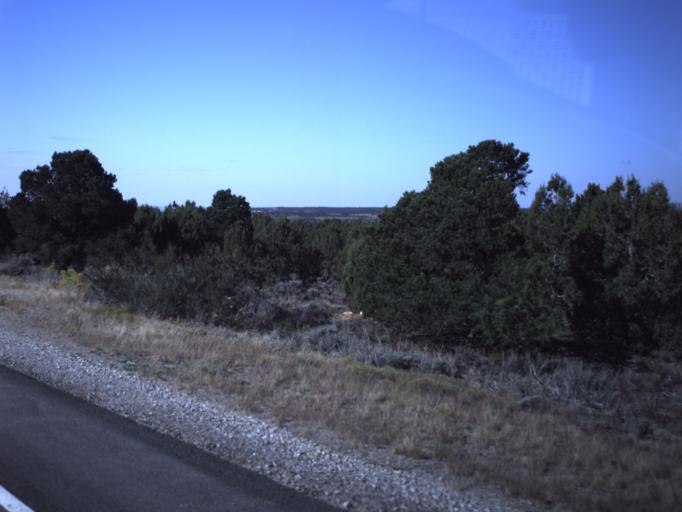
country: US
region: Utah
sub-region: San Juan County
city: Blanding
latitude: 37.6937
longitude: -109.4301
